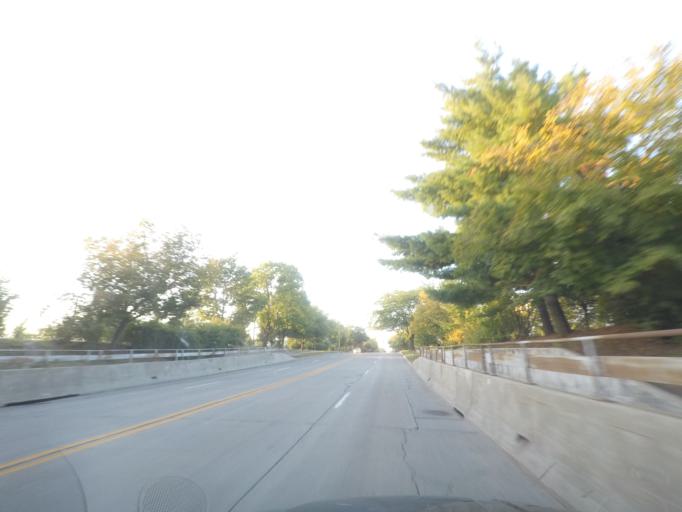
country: US
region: Iowa
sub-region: Story County
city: Ames
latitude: 42.0323
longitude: -93.6447
